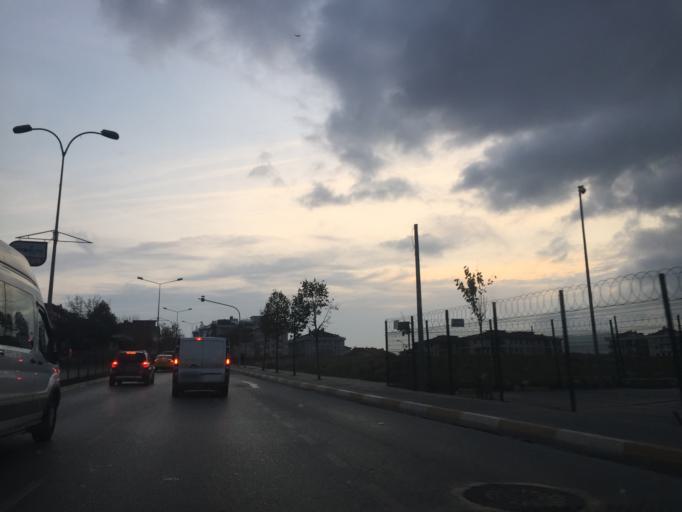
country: TR
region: Istanbul
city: Samandira
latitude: 40.9866
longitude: 29.2241
